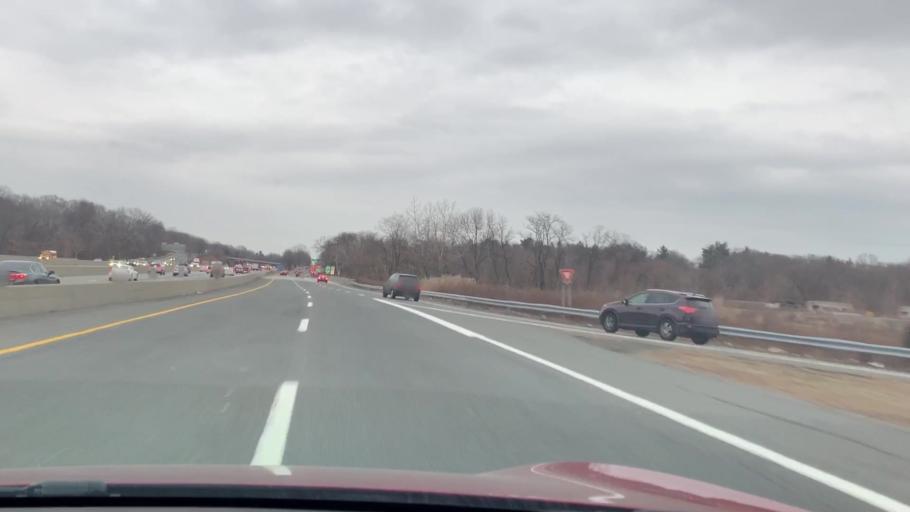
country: US
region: New York
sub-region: Westchester County
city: Purchase
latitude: 41.0139
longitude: -73.7193
